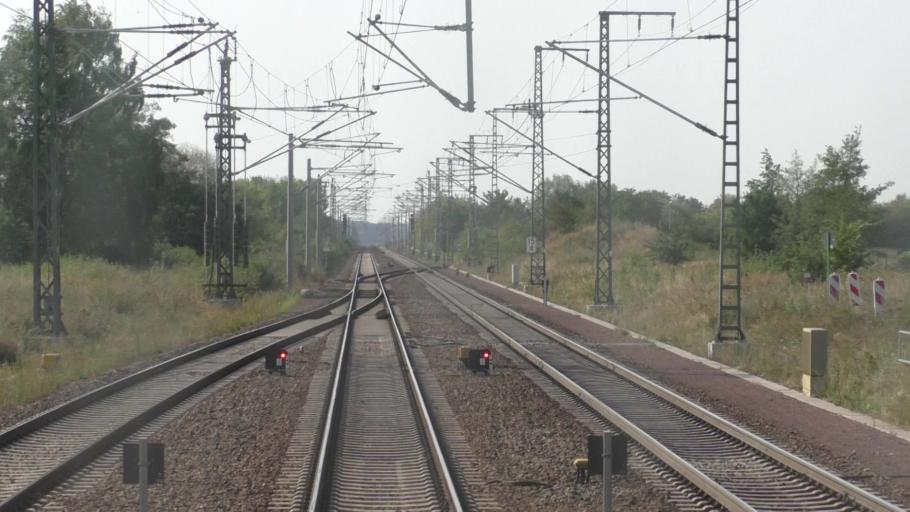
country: DE
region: Saxony-Anhalt
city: Rodleben
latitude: 51.8983
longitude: 12.2154
